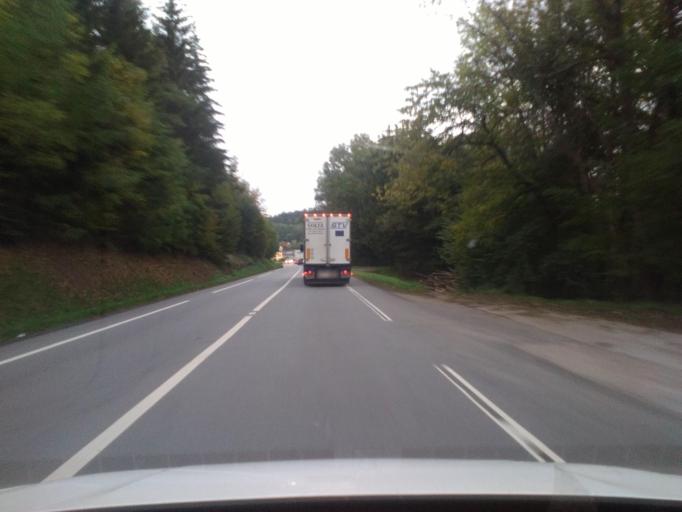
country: FR
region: Lorraine
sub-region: Departement des Vosges
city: Ban-de-Laveline
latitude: 48.2964
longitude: 7.0718
